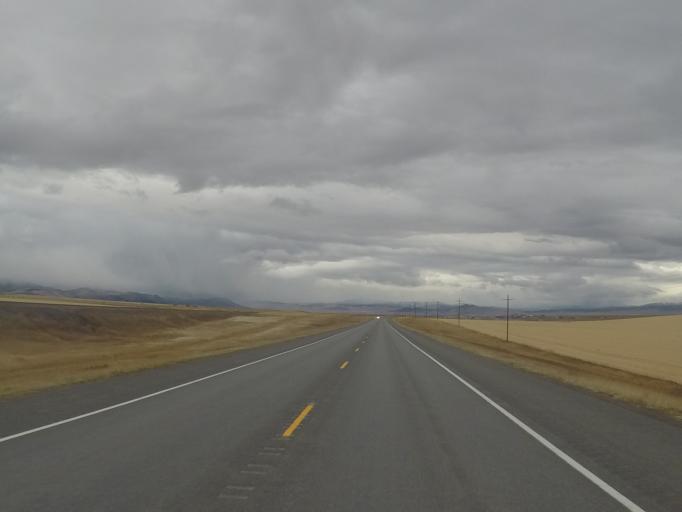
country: US
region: Montana
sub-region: Lewis and Clark County
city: East Helena
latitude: 46.5672
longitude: -111.8093
